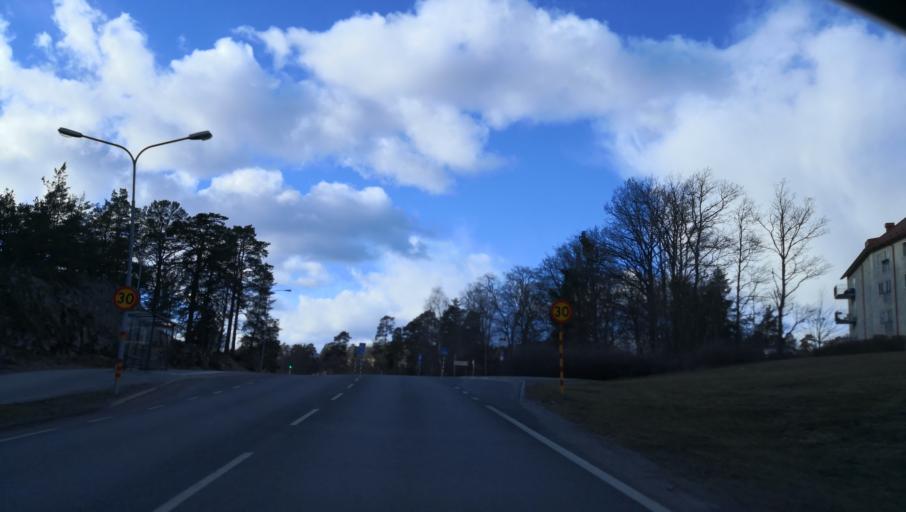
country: SE
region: Stockholm
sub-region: Varmdo Kommun
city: Gustavsberg
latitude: 59.3319
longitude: 18.3890
